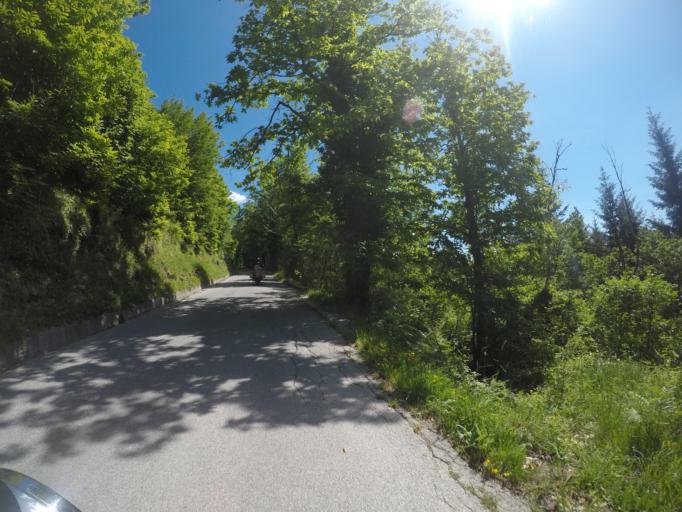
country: IT
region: Tuscany
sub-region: Provincia di Lucca
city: Careggine
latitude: 44.0987
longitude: 10.3274
